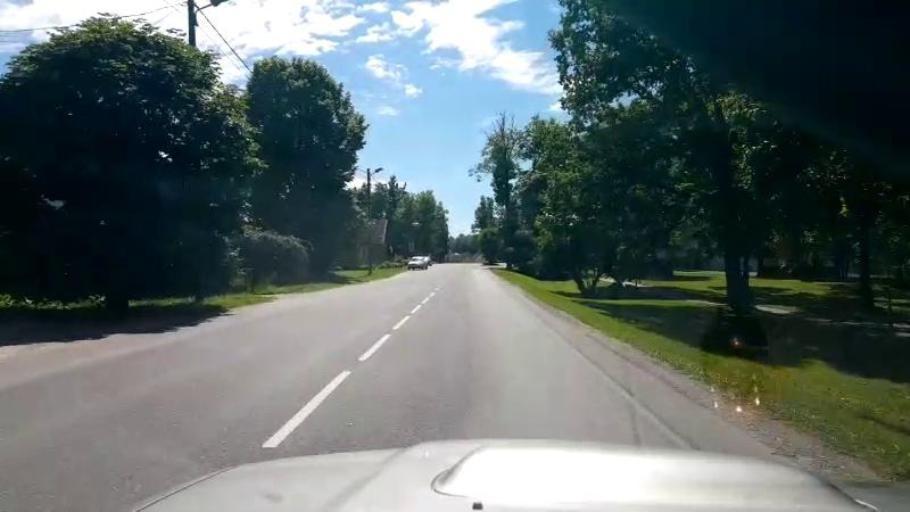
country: EE
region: Jaervamaa
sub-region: Jaerva-Jaani vald
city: Jarva-Jaani
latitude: 59.0388
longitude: 25.8803
